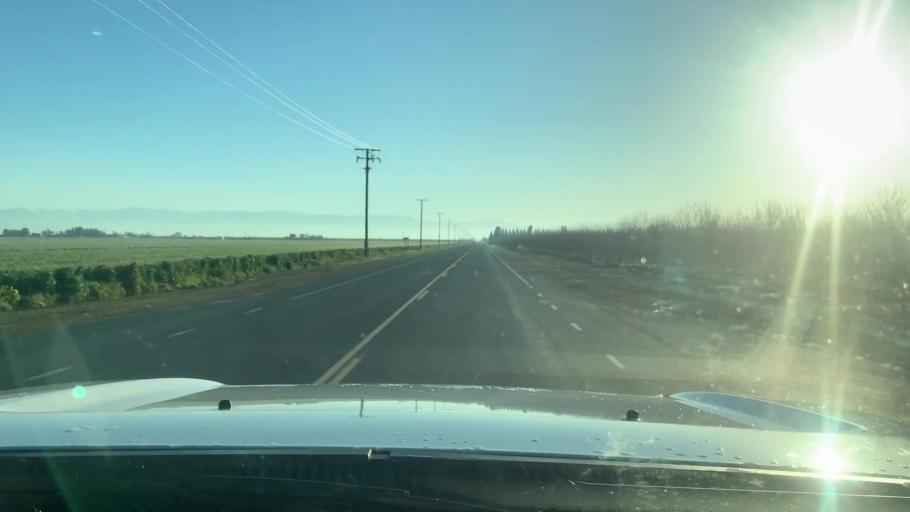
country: US
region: California
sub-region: Kings County
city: Corcoran
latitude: 36.2110
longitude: -119.5107
